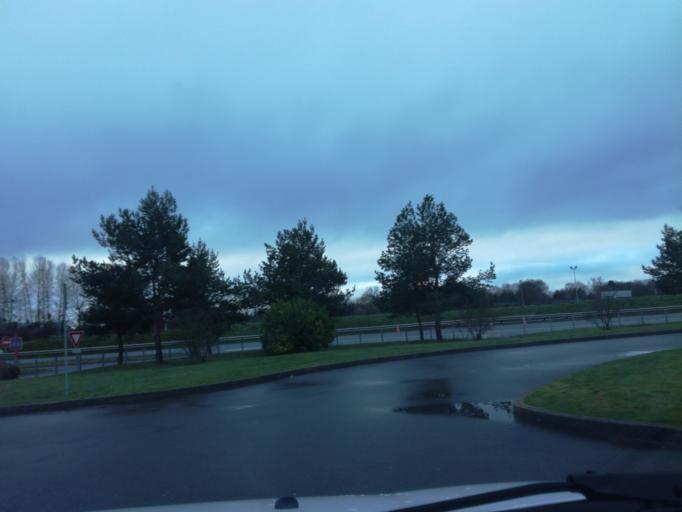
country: FR
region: Brittany
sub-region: Departement d'Ille-et-Vilaine
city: Saint-Jacques-de-la-Lande
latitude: 48.0569
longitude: -1.7294
